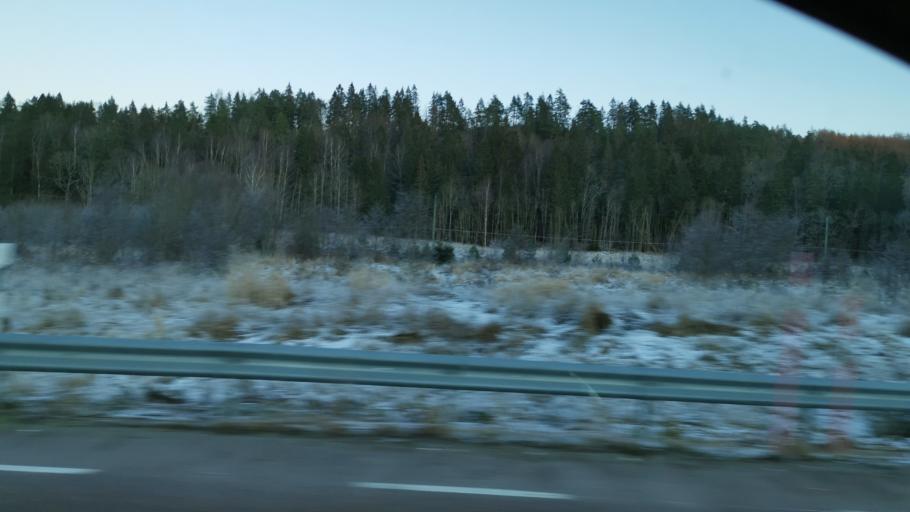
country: SE
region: Vaestra Goetaland
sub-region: Munkedals Kommun
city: Munkedal
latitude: 58.4235
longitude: 11.7250
